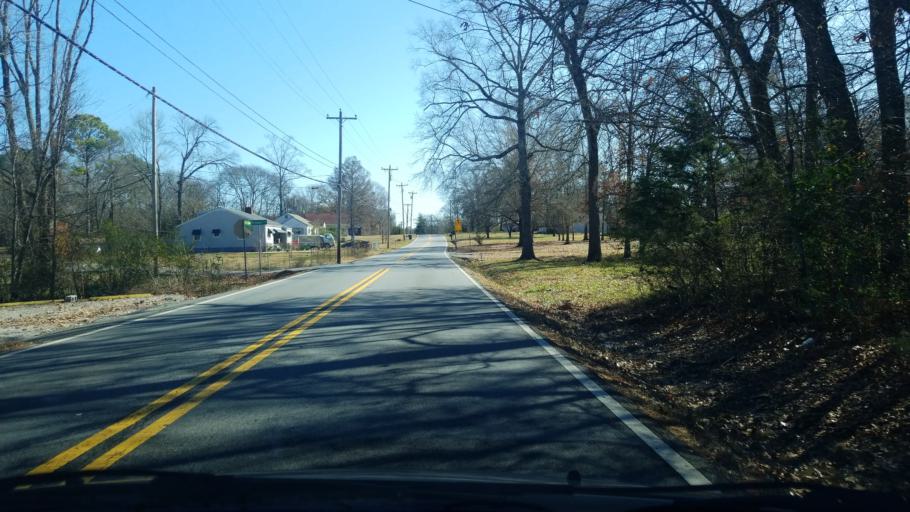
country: US
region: Georgia
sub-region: Catoosa County
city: Fort Oglethorpe
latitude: 34.9614
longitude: -85.2496
